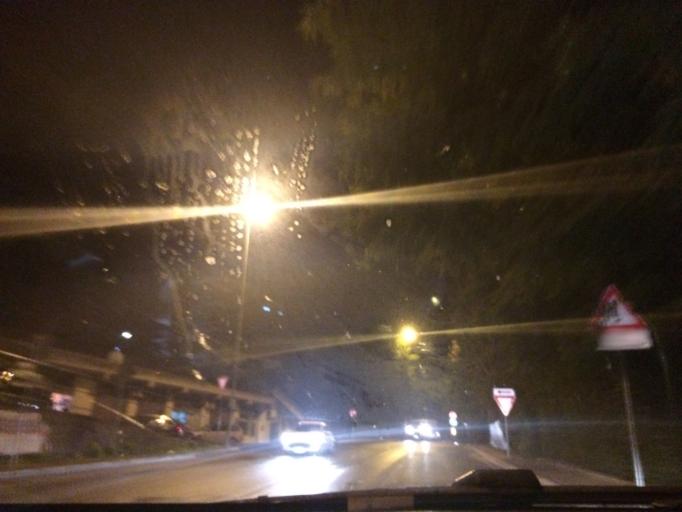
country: IT
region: Basilicate
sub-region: Provincia di Matera
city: Matera
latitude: 40.6618
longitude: 16.5970
